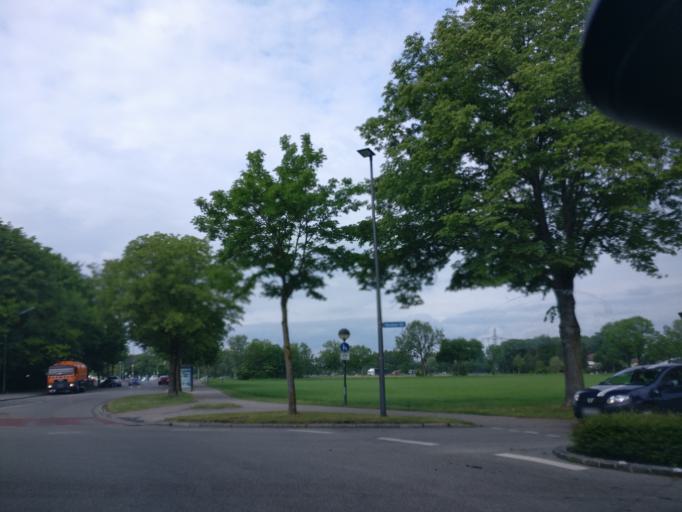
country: DE
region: Bavaria
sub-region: Upper Bavaria
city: Karlsfeld
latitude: 48.2293
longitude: 11.4646
